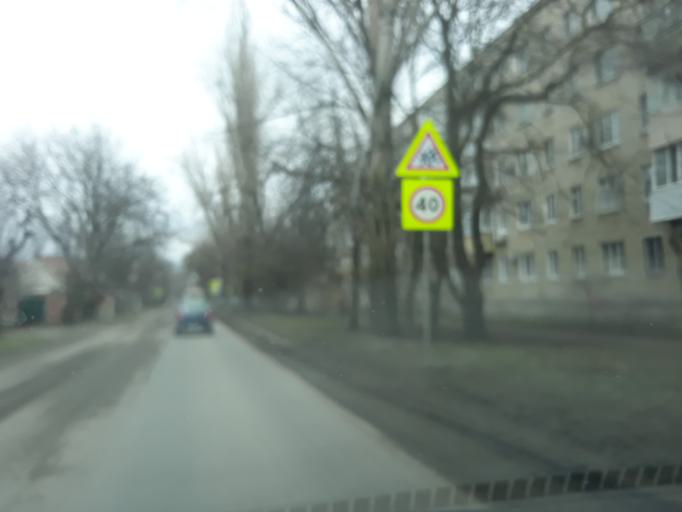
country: RU
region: Rostov
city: Taganrog
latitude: 47.2654
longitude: 38.9182
